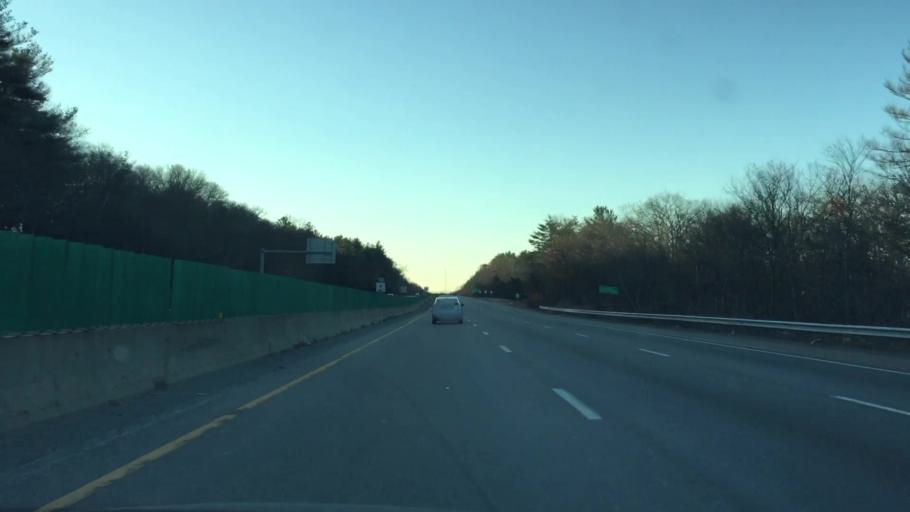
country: US
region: Massachusetts
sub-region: Plymouth County
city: Brockton
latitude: 42.0517
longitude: -71.0584
